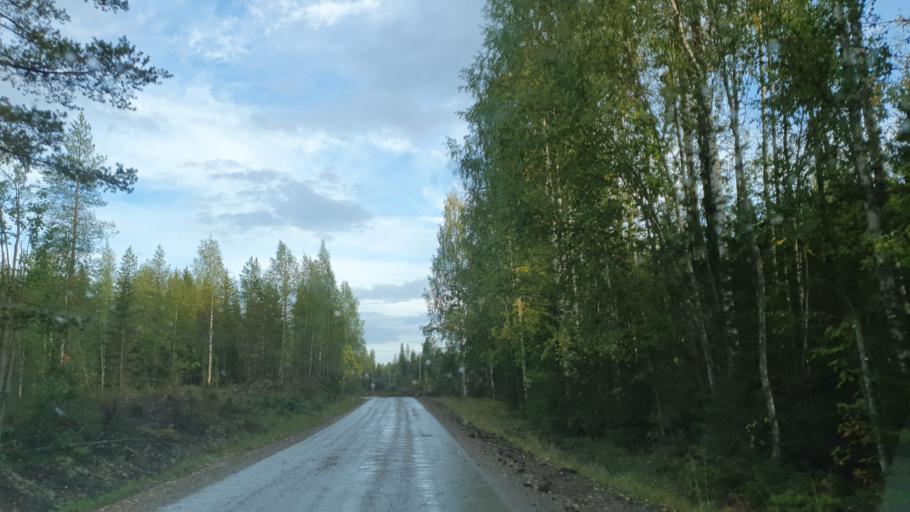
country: FI
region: Kainuu
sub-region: Kehys-Kainuu
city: Kuhmo
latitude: 64.3876
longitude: 29.4257
